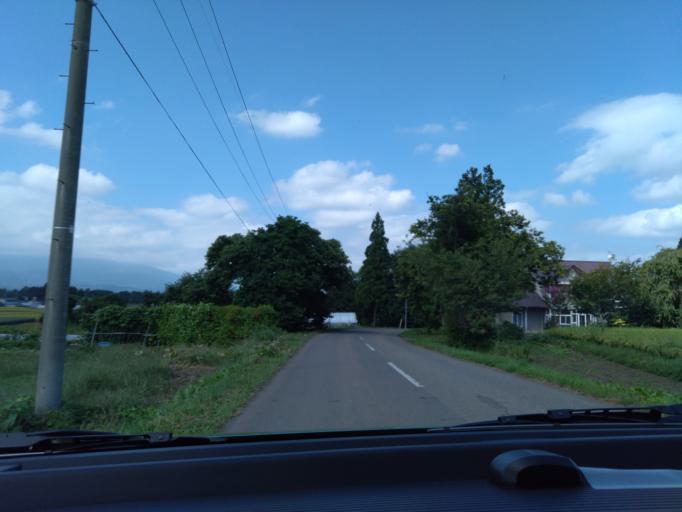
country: JP
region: Iwate
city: Shizukuishi
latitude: 39.6811
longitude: 140.9591
